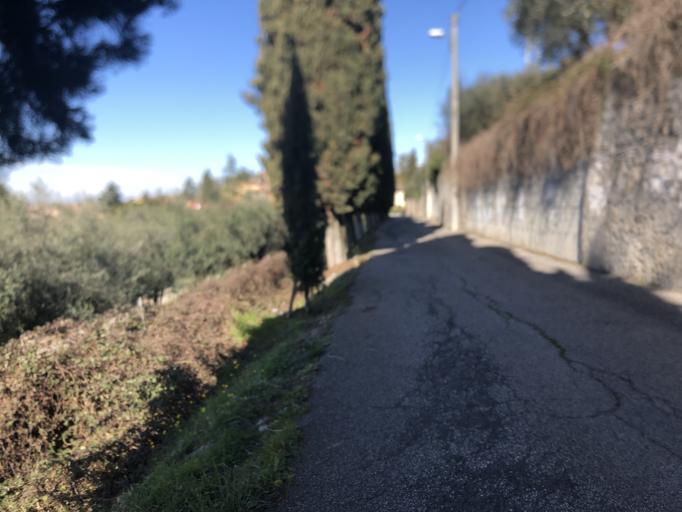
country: IT
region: Veneto
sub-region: Provincia di Verona
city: Sona
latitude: 45.4310
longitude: 10.8355
